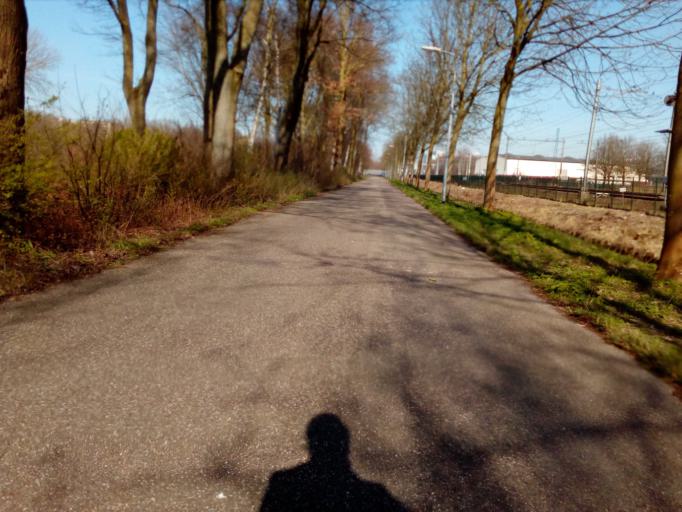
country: NL
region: South Holland
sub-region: Gemeente Rijswijk
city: Rijswijk
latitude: 52.0292
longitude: 4.3322
